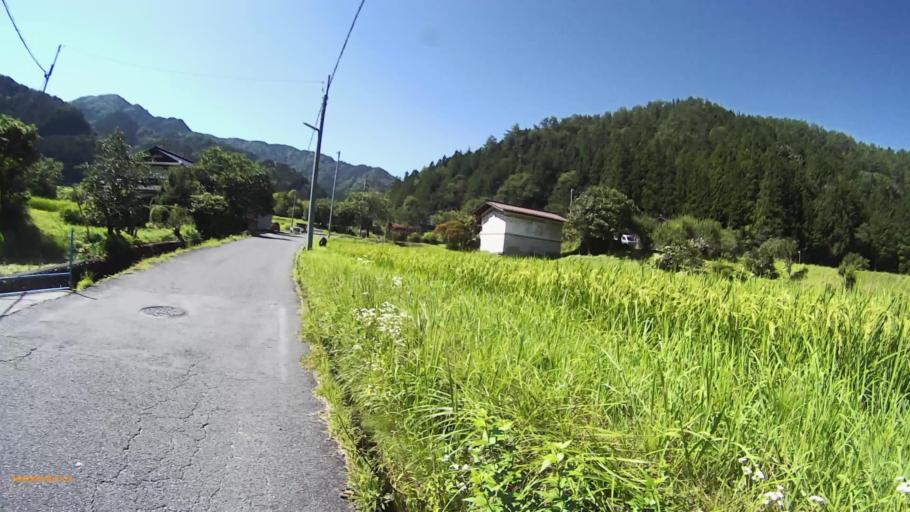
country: JP
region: Nagano
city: Iida
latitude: 35.6853
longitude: 137.6746
